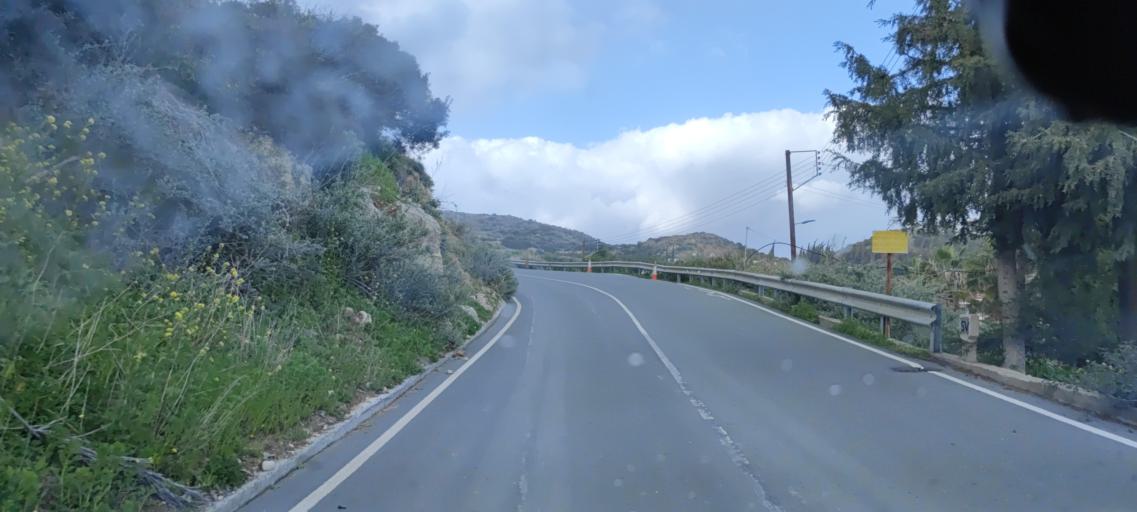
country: CY
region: Limassol
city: Pissouri
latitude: 34.6518
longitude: 32.7231
